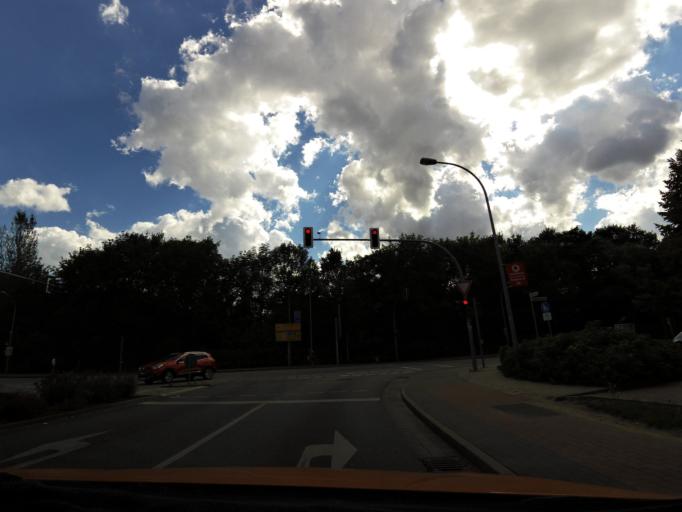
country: DE
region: Brandenburg
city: Konigs Wusterhausen
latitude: 52.2987
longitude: 13.6290
